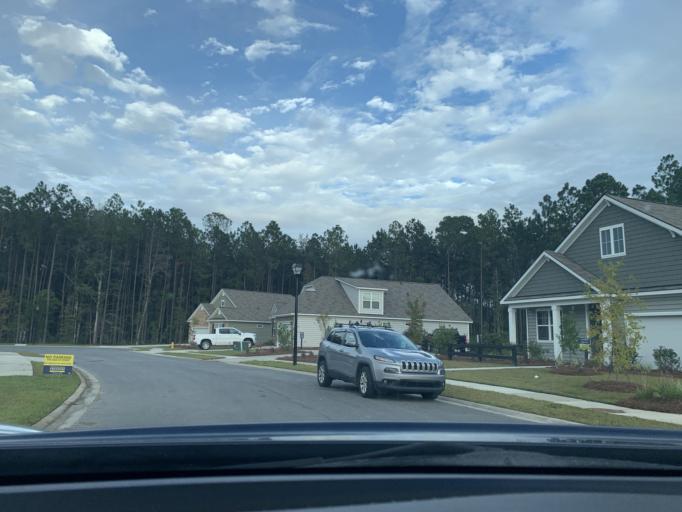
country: US
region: Georgia
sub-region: Chatham County
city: Pooler
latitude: 32.0694
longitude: -81.2570
